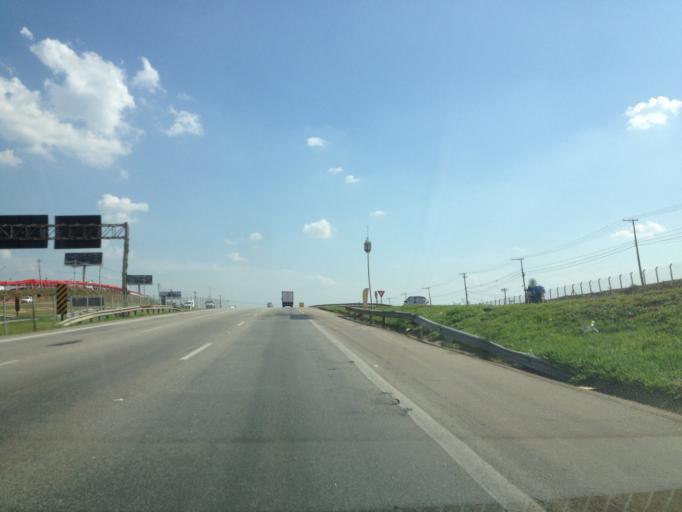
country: BR
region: Sao Paulo
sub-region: Campinas
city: Campinas
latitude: -23.0075
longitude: -47.1142
